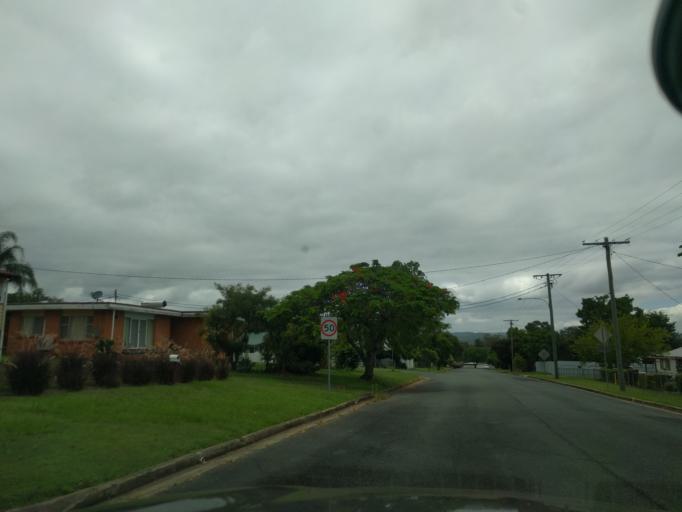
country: AU
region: Queensland
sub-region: Logan
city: Cedar Vale
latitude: -27.9898
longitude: 153.0044
